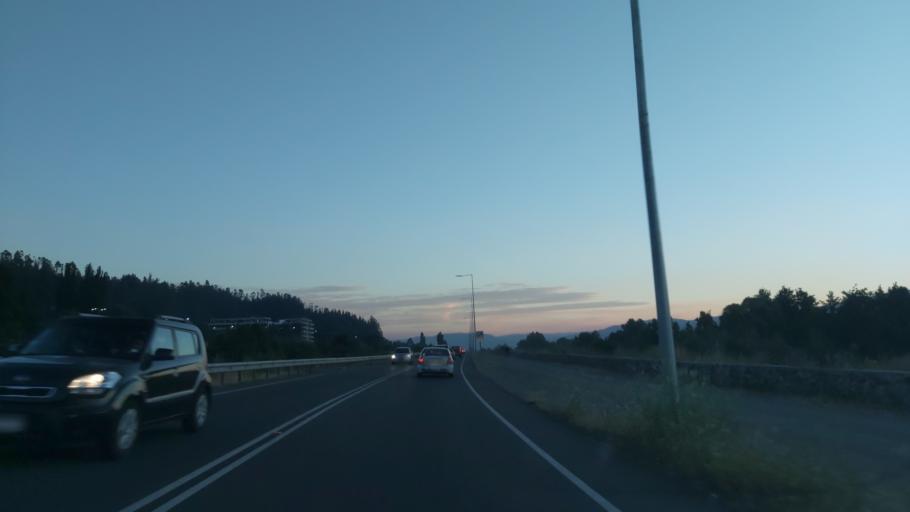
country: CL
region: Biobio
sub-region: Provincia de Concepcion
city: Chiguayante
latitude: -36.8787
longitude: -73.0391
